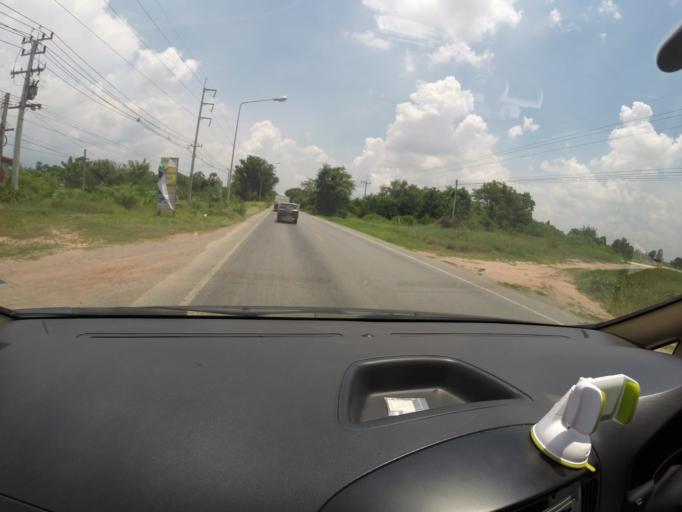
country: TH
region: Nakhon Ratchasima
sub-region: Amphoe Thepharak
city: Thepharak
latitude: 15.1223
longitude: 101.5173
